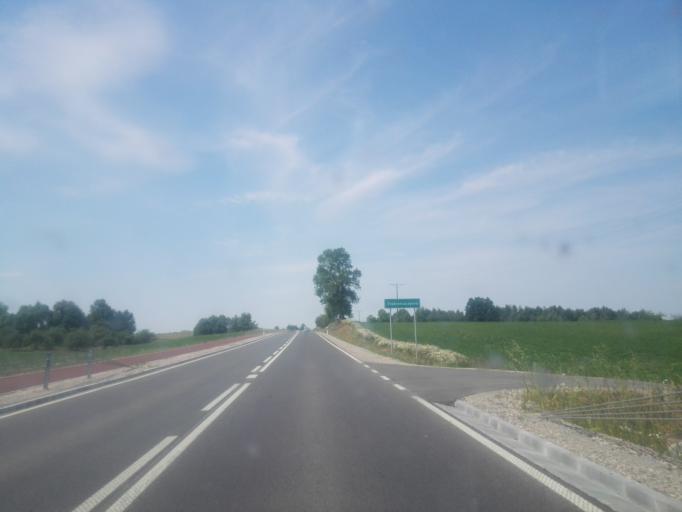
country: PL
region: Podlasie
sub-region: Powiat sejnenski
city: Sejny
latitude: 54.1091
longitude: 23.2956
